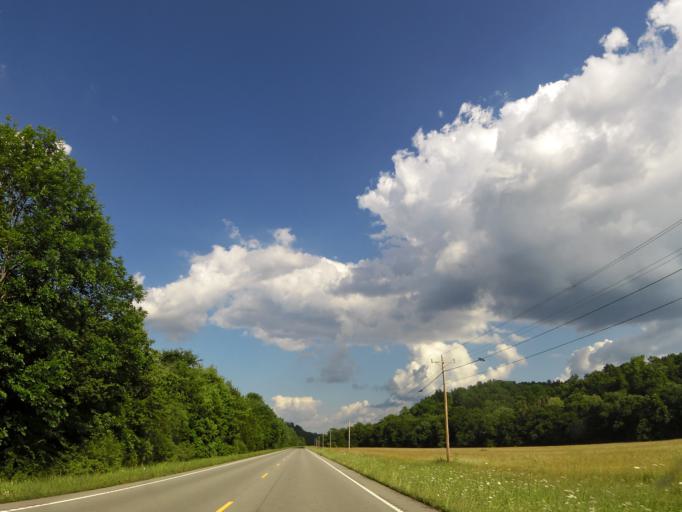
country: US
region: Tennessee
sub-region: Perry County
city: Linden
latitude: 35.6151
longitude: -87.7272
